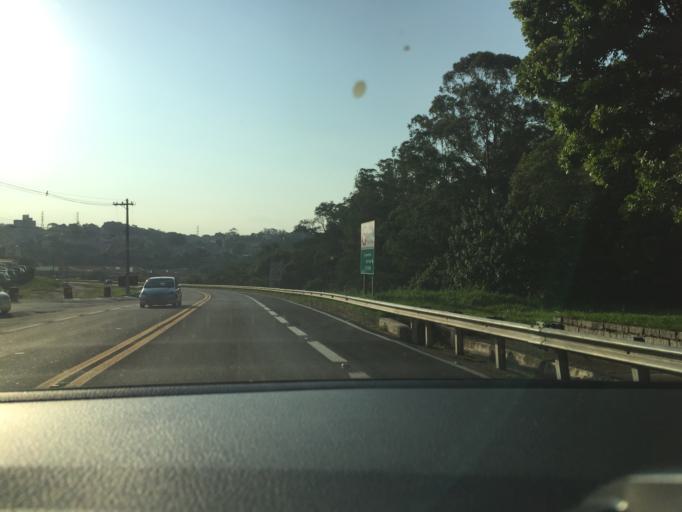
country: BR
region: Sao Paulo
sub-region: Louveira
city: Louveira
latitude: -23.0875
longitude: -46.9441
